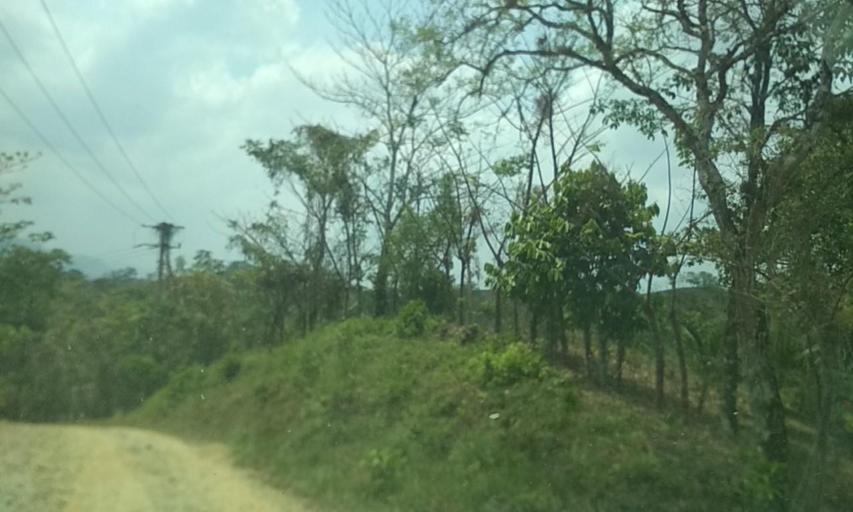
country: MX
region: Tabasco
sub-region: Huimanguillo
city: Francisco Rueda
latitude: 17.6070
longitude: -93.8070
